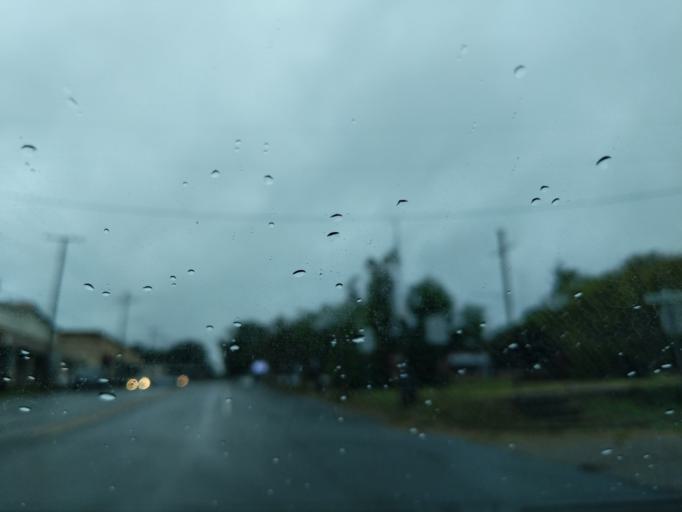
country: US
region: Louisiana
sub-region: Bienville Parish
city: Arcadia
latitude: 32.5460
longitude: -93.0530
